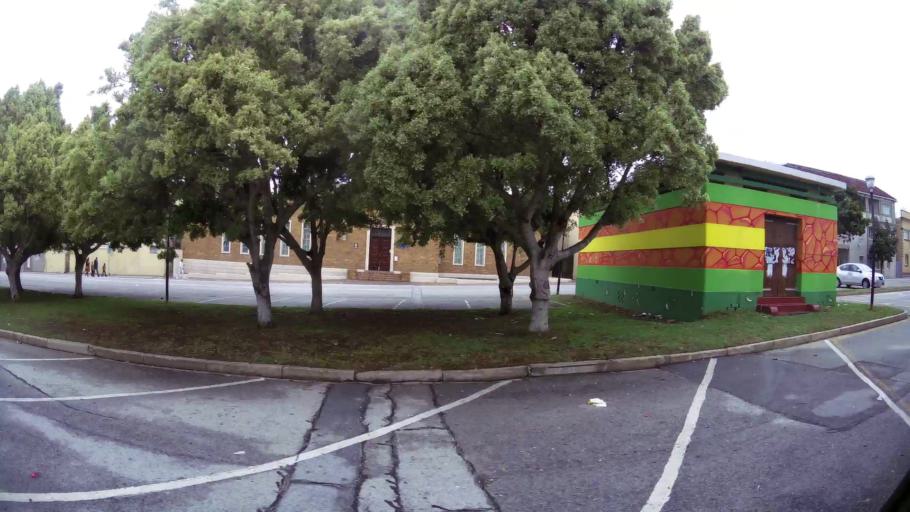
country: ZA
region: Eastern Cape
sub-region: Nelson Mandela Bay Metropolitan Municipality
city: Port Elizabeth
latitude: -33.9615
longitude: 25.6173
